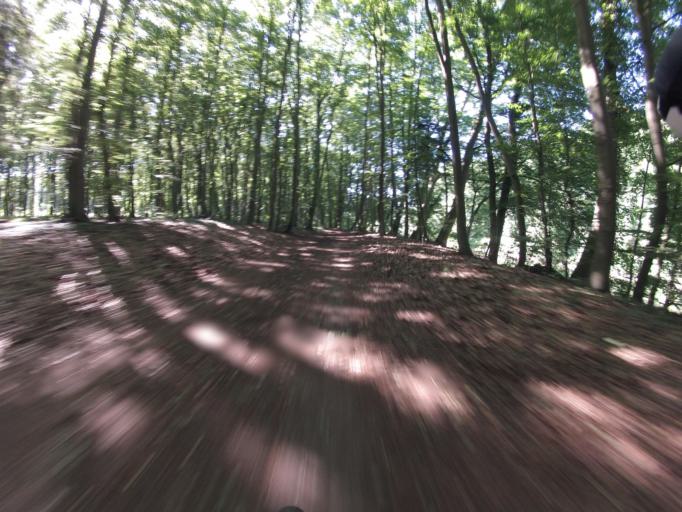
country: DE
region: North Rhine-Westphalia
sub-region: Regierungsbezirk Munster
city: Rheine
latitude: 52.3053
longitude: 7.4294
